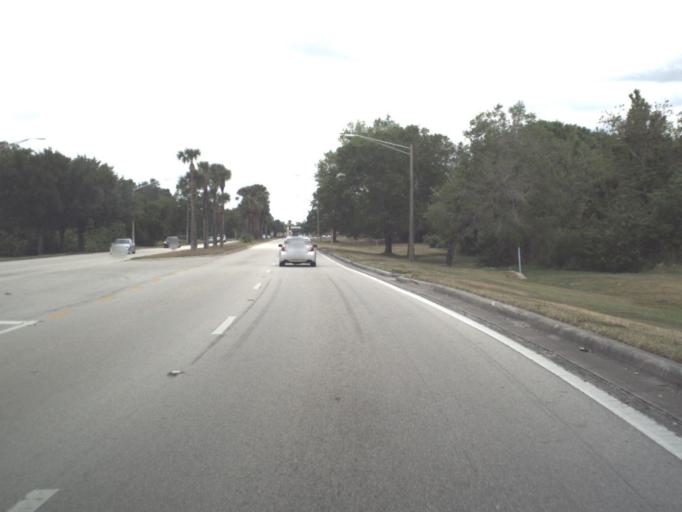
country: US
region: Florida
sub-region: Orange County
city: Belle Isle
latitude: 28.4438
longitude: -81.3335
